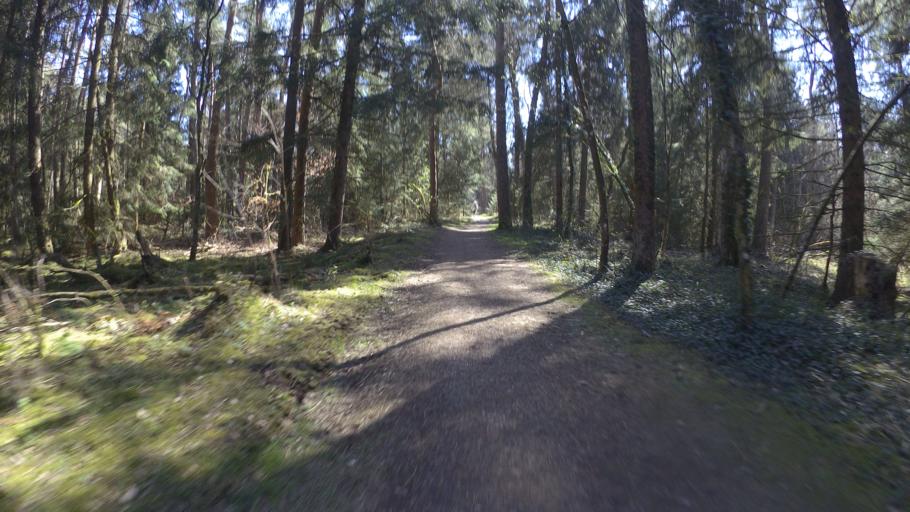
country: DE
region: Bavaria
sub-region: Upper Bavaria
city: Seeon-Seebruck
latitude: 47.9360
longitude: 12.4871
